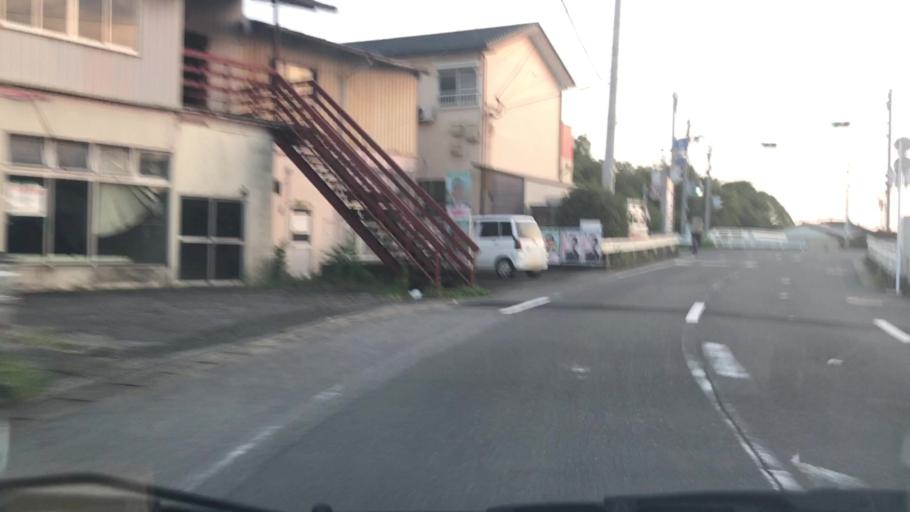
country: JP
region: Saga Prefecture
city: Saga-shi
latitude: 33.2561
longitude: 130.2889
